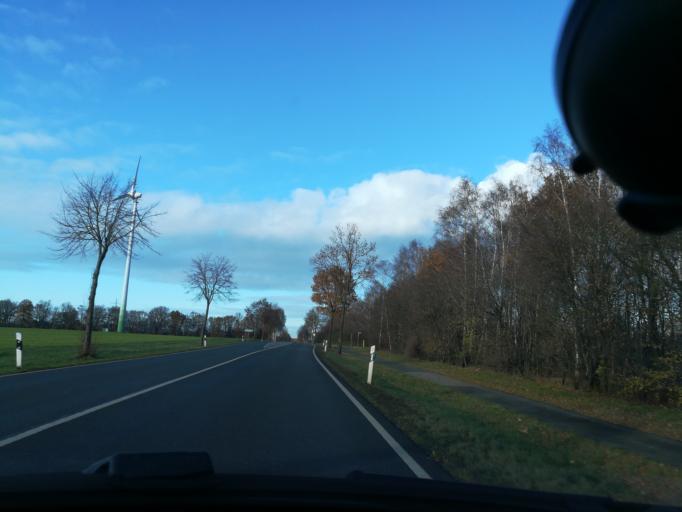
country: DE
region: Lower Saxony
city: Uchte
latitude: 52.4791
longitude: 8.8955
